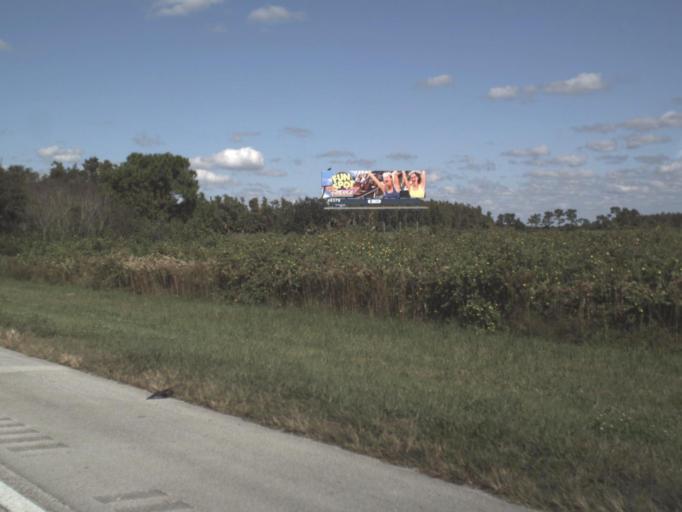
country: US
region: Florida
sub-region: Osceola County
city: Saint Cloud
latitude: 28.0464
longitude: -81.2135
